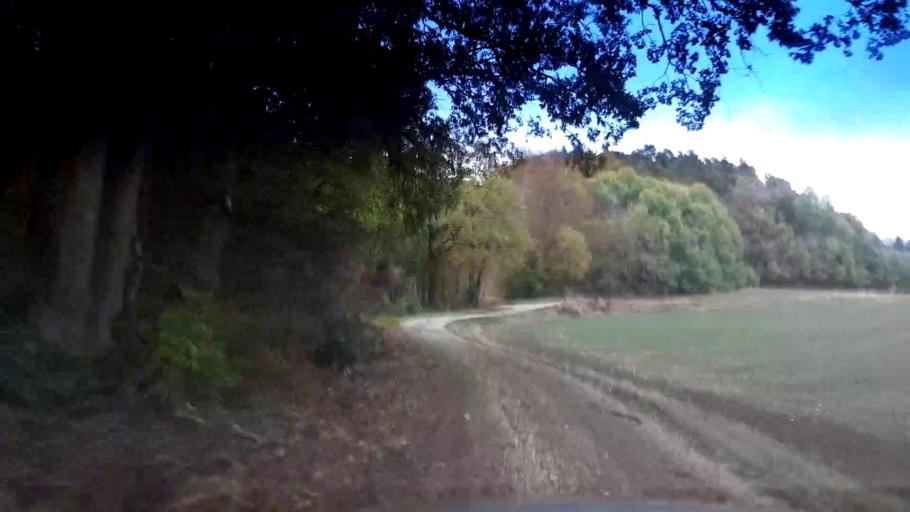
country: DE
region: Bavaria
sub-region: Upper Franconia
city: Schesslitz
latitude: 49.9540
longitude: 11.0404
